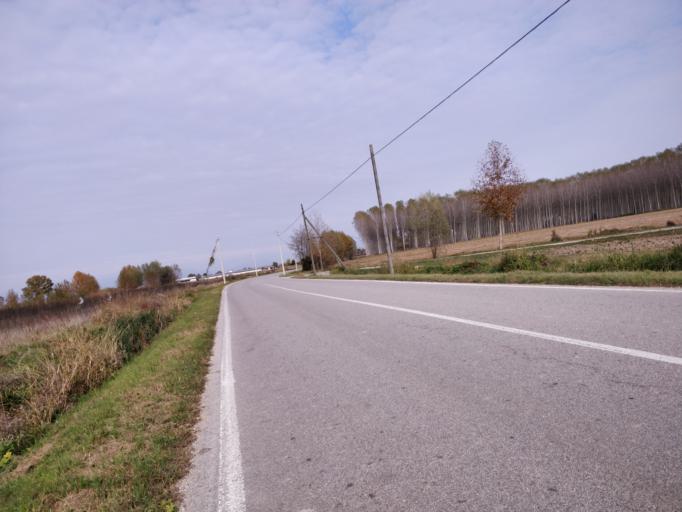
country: IT
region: Friuli Venezia Giulia
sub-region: Provincia di Udine
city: Bertiolo
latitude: 45.9279
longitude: 13.0486
